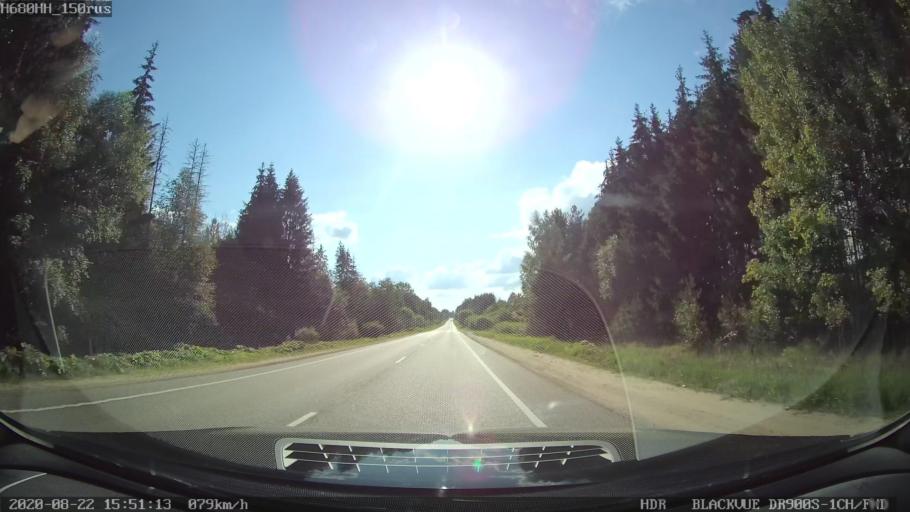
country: RU
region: Tverskaya
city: Bezhetsk
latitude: 57.6663
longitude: 36.4303
